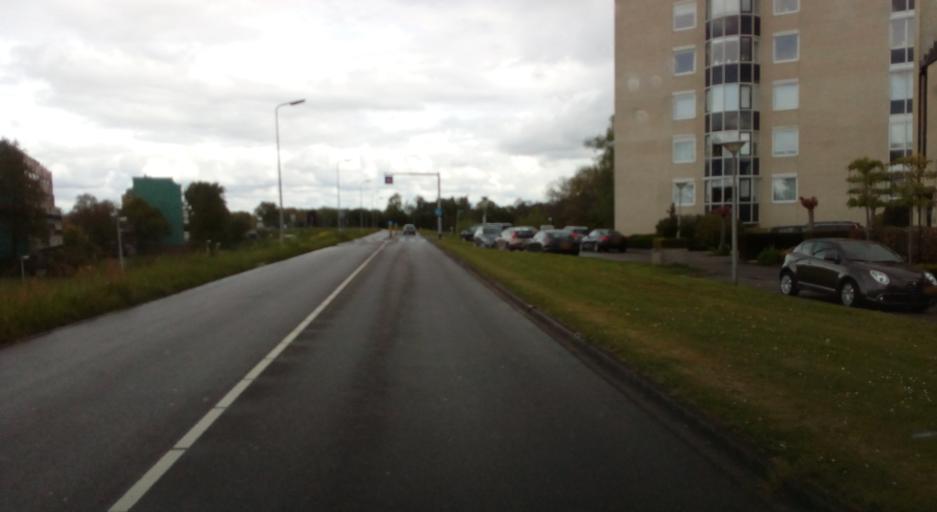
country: NL
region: South Holland
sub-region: Gemeente Dordrecht
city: Dordrecht
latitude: 51.8230
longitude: 4.6621
